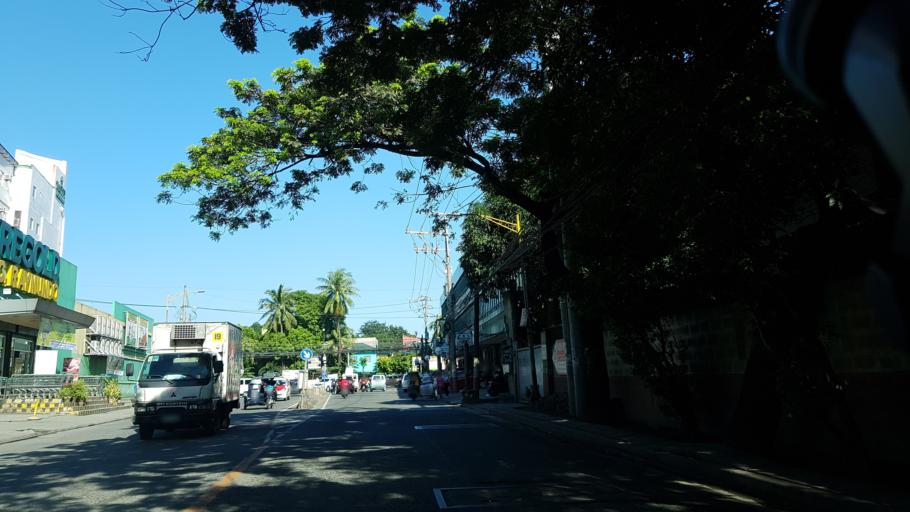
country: PH
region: Metro Manila
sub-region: Pasig
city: Pasig City
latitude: 14.5759
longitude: 121.0860
